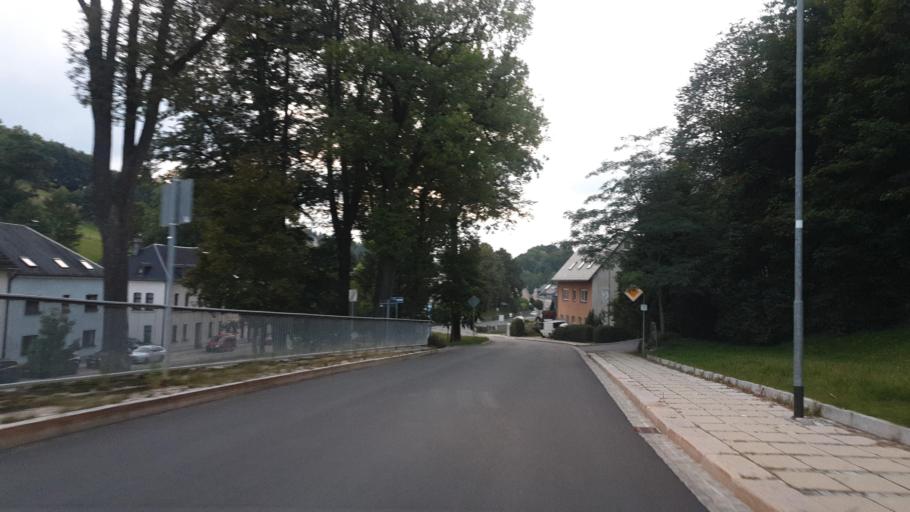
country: DE
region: Saxony
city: Eibenstock
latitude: 50.4959
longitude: 12.5919
